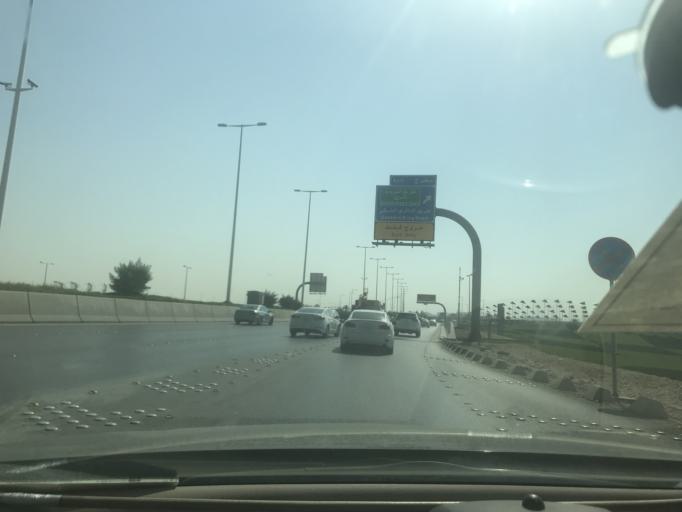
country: SA
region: Ar Riyad
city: Riyadh
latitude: 24.7281
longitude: 46.7097
